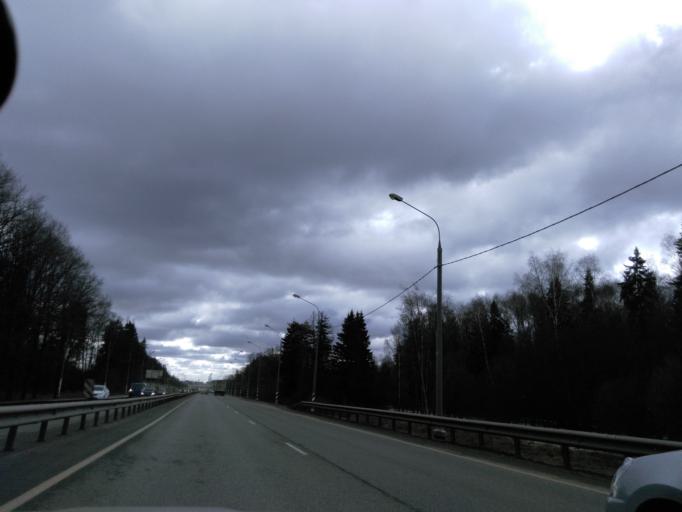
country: RU
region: Moskovskaya
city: Rzhavki
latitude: 56.0072
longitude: 37.2255
